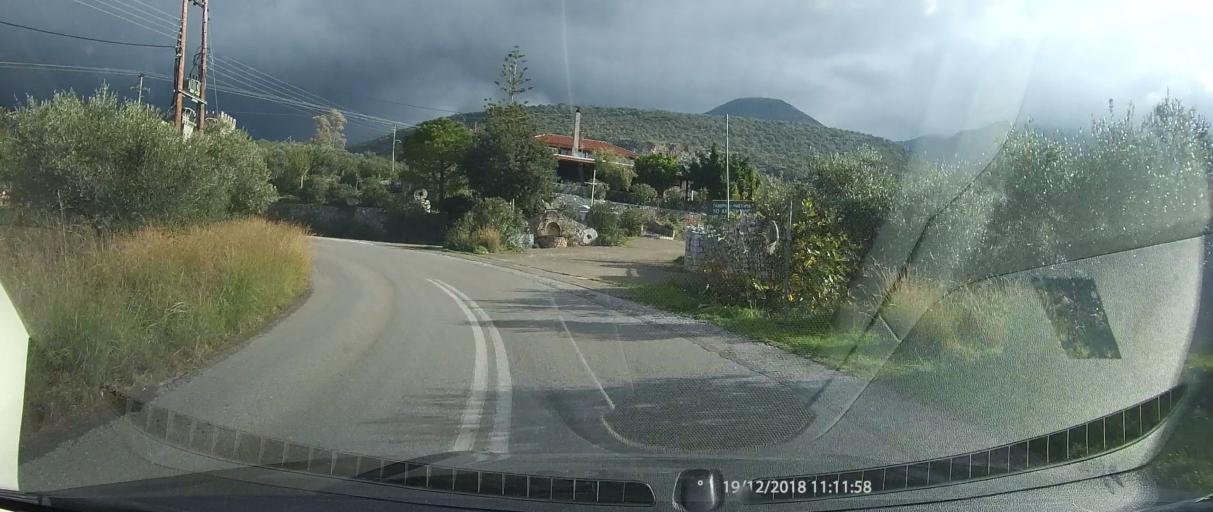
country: GR
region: Peloponnese
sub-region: Nomos Messinias
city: Kardamyli
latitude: 36.8187
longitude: 22.3049
